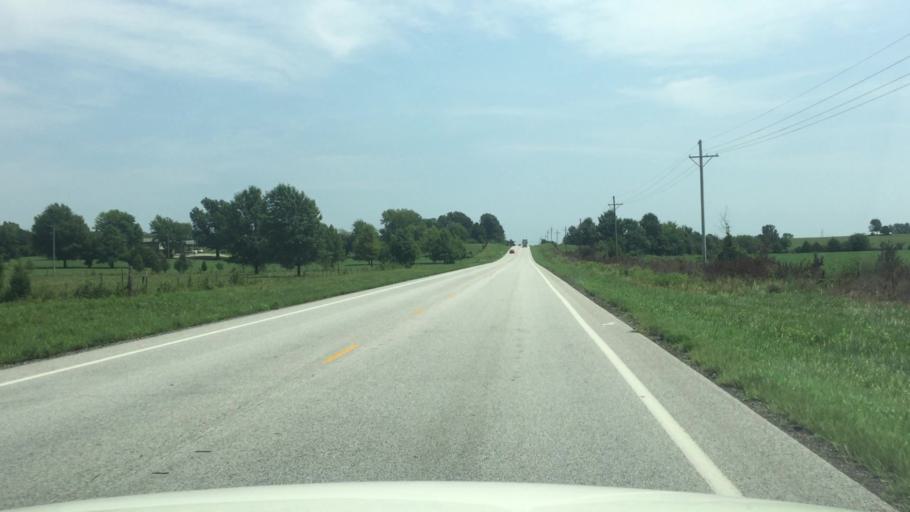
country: US
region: Kansas
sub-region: Cherokee County
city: Columbus
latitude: 37.1780
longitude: -94.7948
